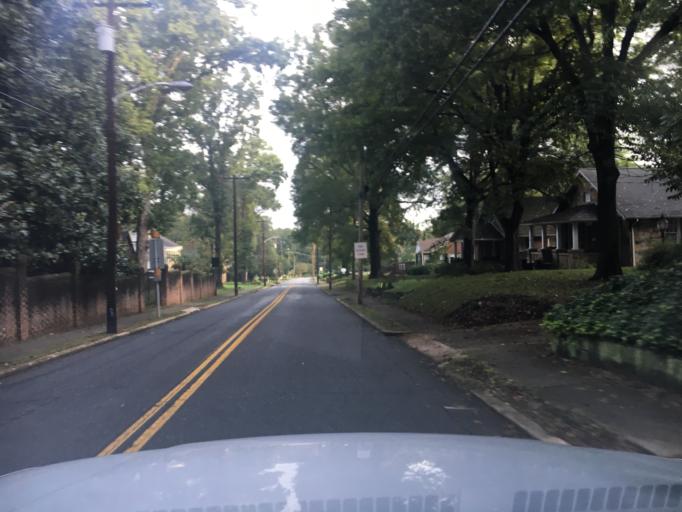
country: US
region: North Carolina
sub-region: Catawba County
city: Hickory
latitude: 35.7382
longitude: -81.3444
